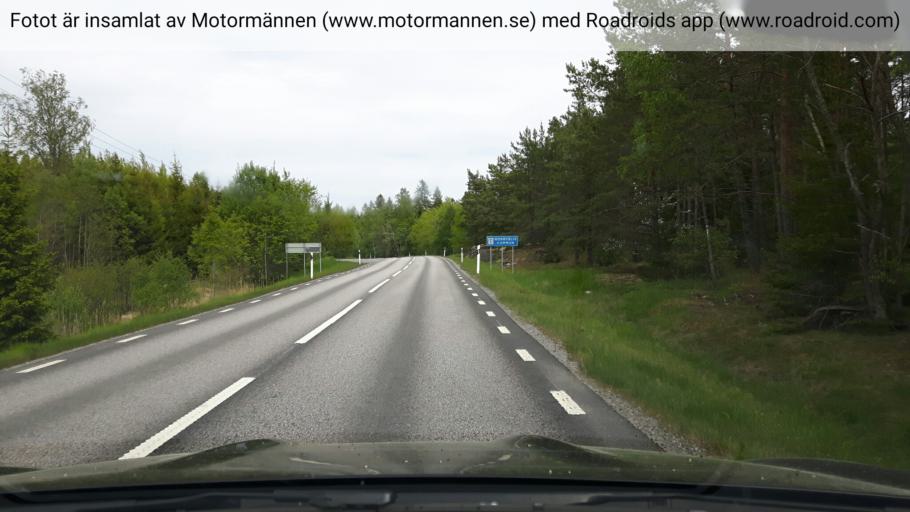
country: SE
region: Stockholm
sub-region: Norrtalje Kommun
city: Norrtalje
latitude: 59.5814
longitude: 18.6559
